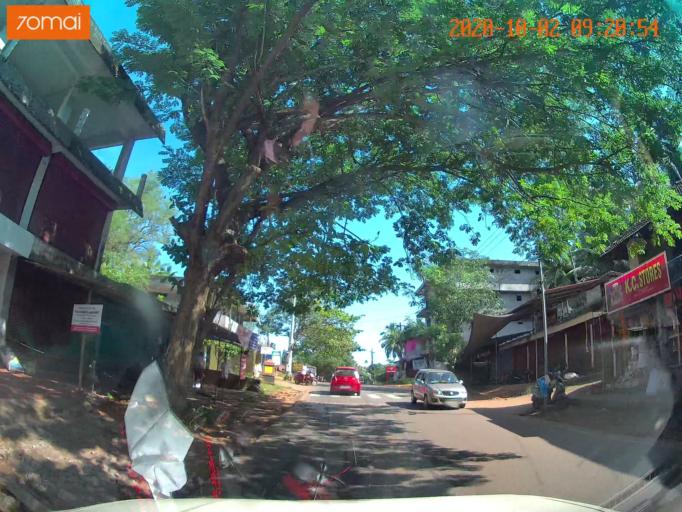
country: IN
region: Kerala
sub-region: Kozhikode
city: Naduvannur
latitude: 11.5700
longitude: 75.7537
